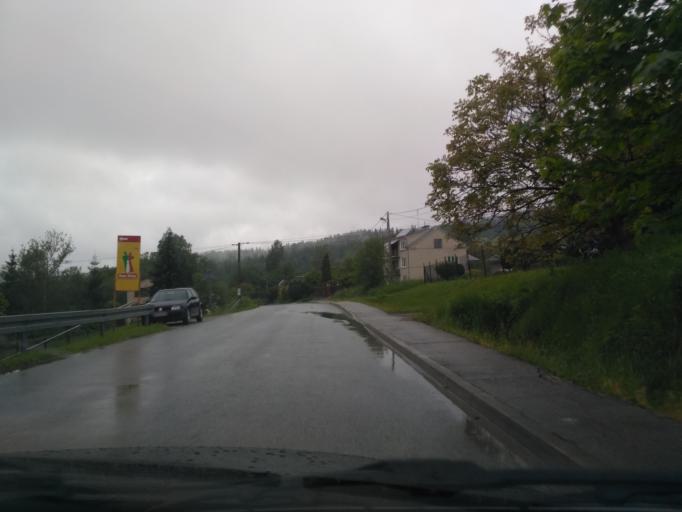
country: PL
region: Lesser Poland Voivodeship
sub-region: Powiat gorlicki
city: Sekowa
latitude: 49.6204
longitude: 21.2289
